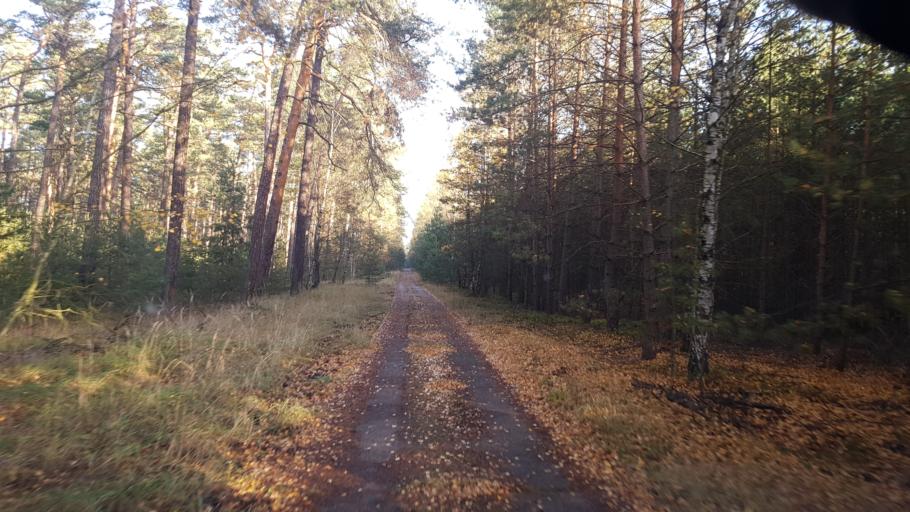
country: DE
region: Brandenburg
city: Crinitz
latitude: 51.7196
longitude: 13.7444
